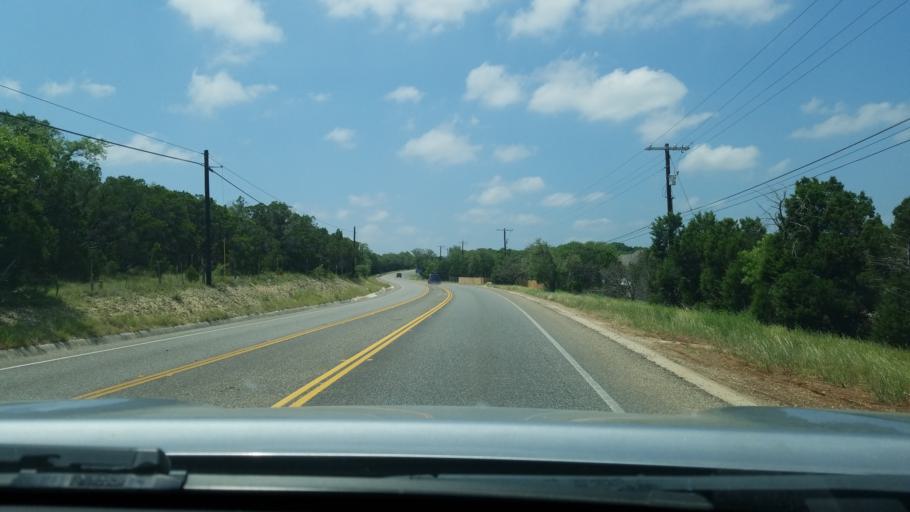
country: US
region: Texas
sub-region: Hays County
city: Woodcreek
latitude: 30.0152
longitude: -98.1234
